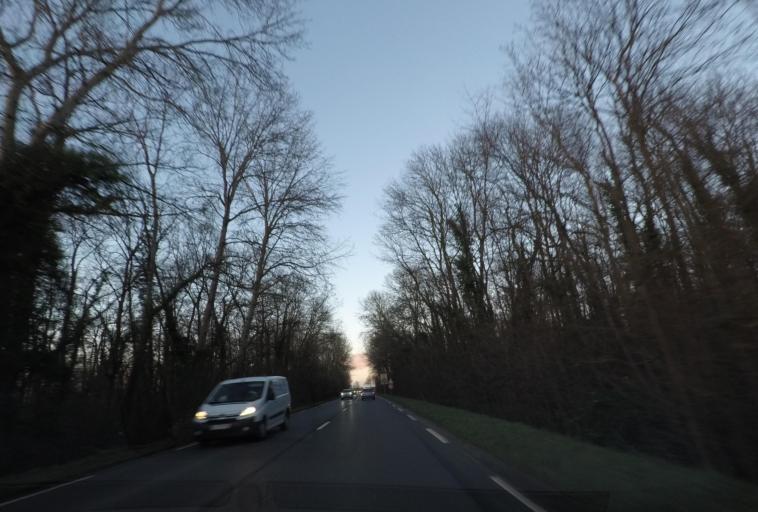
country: FR
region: Ile-de-France
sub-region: Departement de l'Essonne
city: Vert-le-Grand
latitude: 48.5823
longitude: 2.3671
